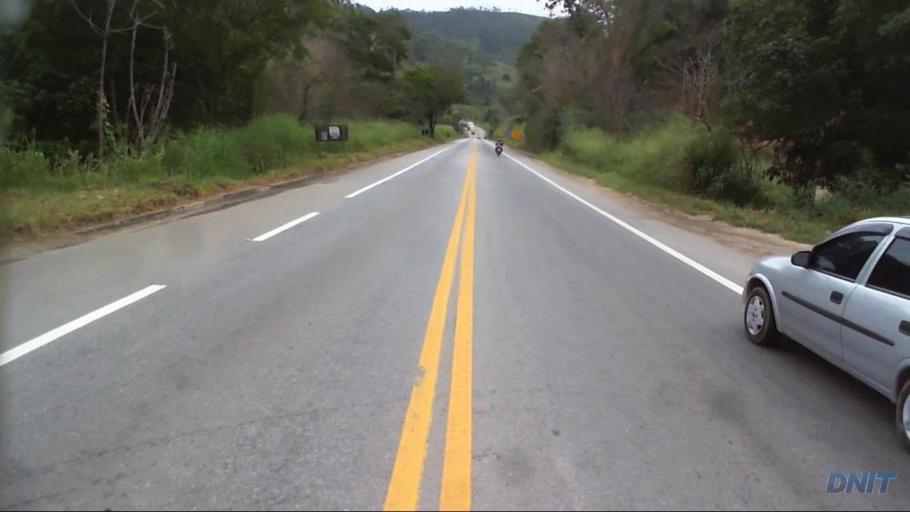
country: BR
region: Minas Gerais
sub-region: Timoteo
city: Timoteo
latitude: -19.6373
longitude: -42.8229
